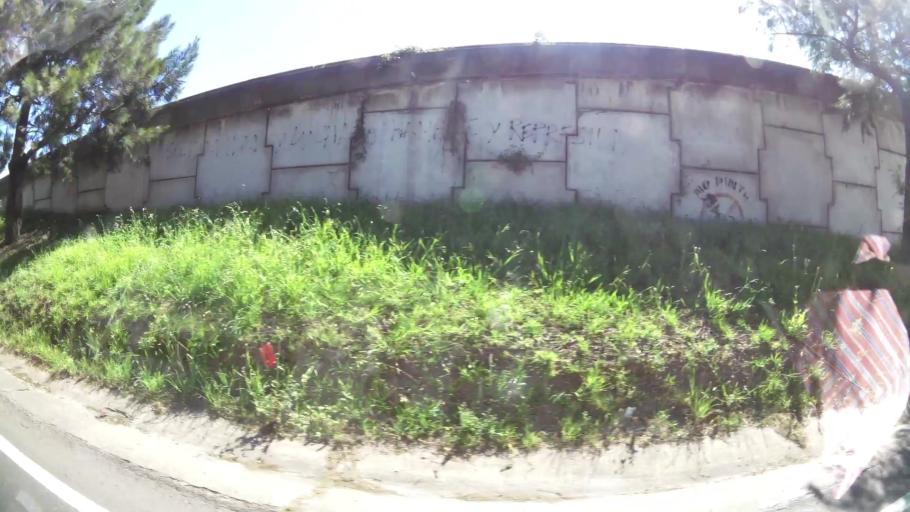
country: AR
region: Buenos Aires
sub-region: Partido de Vicente Lopez
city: Olivos
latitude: -34.5176
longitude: -58.5171
